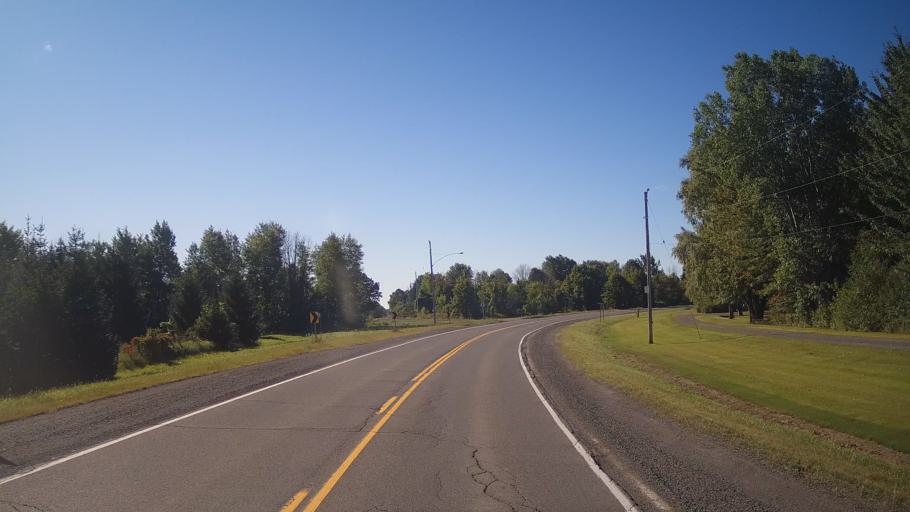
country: CA
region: Ontario
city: Bells Corners
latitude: 45.1064
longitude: -75.6136
